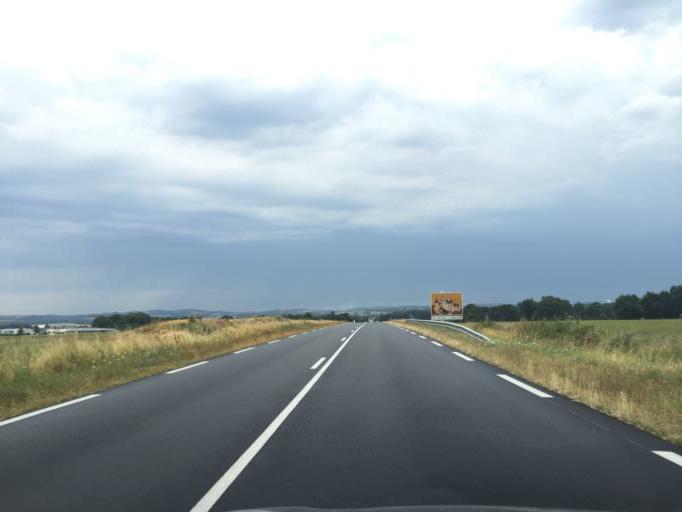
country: FR
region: Auvergne
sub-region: Departement de l'Allier
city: Lapalisse
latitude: 46.2489
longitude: 3.5811
